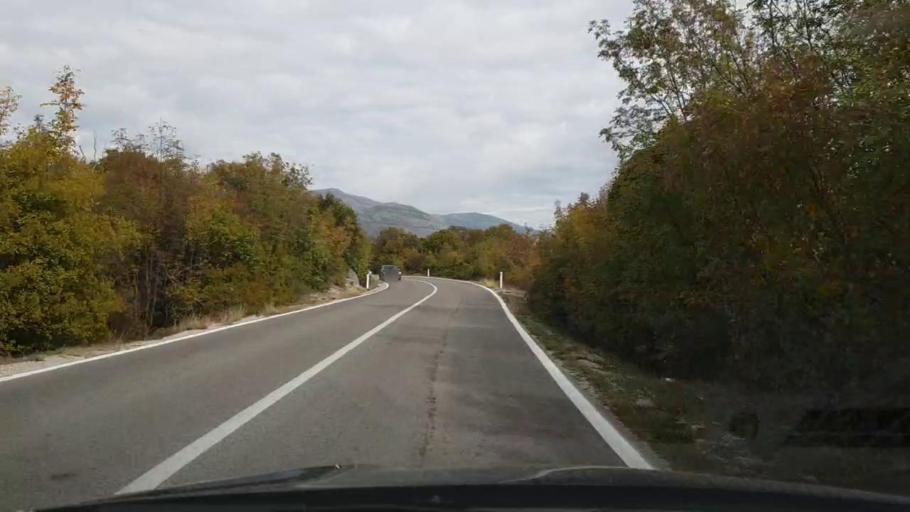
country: HR
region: Dubrovacko-Neretvanska
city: Jasenice
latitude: 42.6860
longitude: 18.2486
